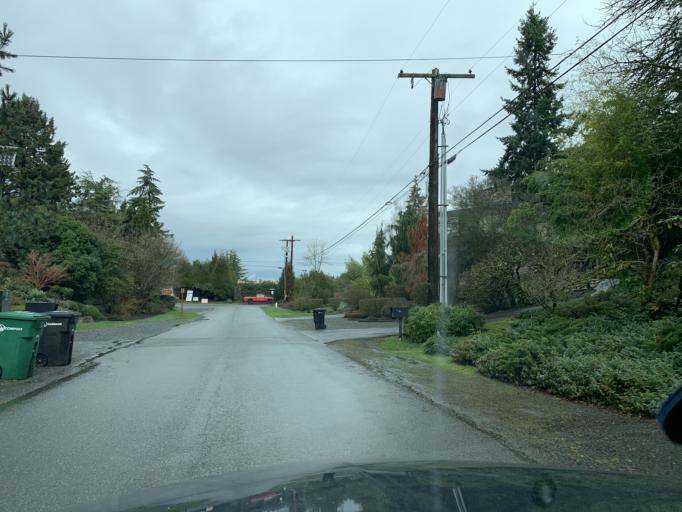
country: US
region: Washington
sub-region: King County
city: Mercer Island
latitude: 47.5920
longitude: -122.2317
